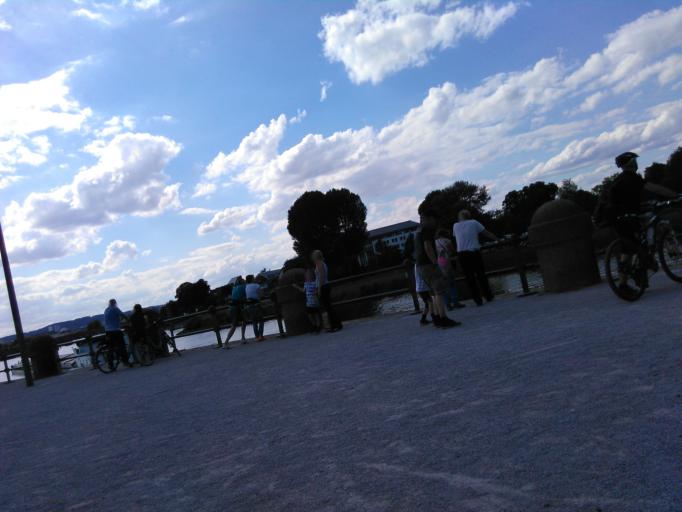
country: DE
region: Rheinland-Pfalz
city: Koblenz
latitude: 50.3649
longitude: 7.6065
